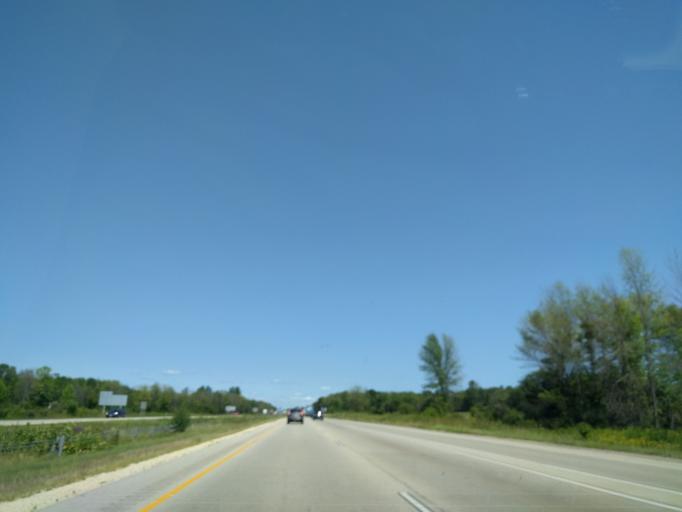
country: US
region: Wisconsin
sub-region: Ozaukee County
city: Grafton
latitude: 43.2831
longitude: -87.9212
